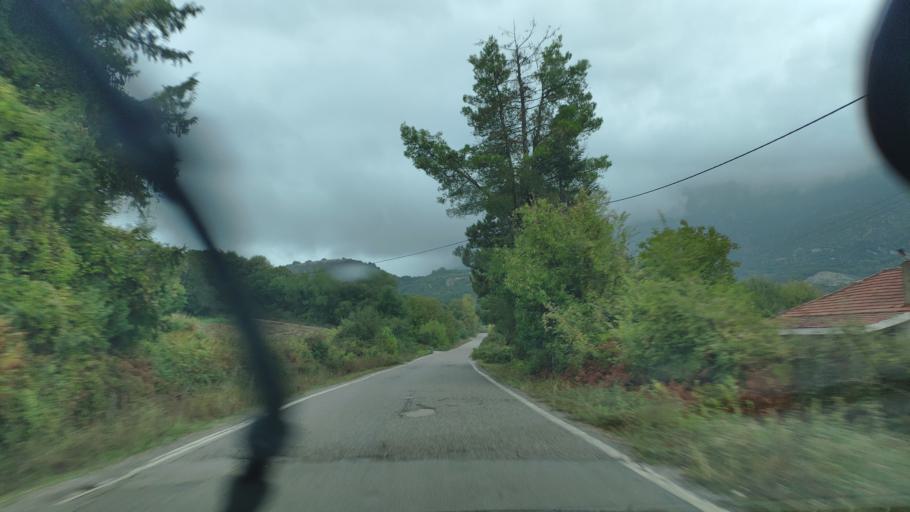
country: GR
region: West Greece
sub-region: Nomos Aitolias kai Akarnanias
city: Krikellos
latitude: 39.0147
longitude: 21.3080
